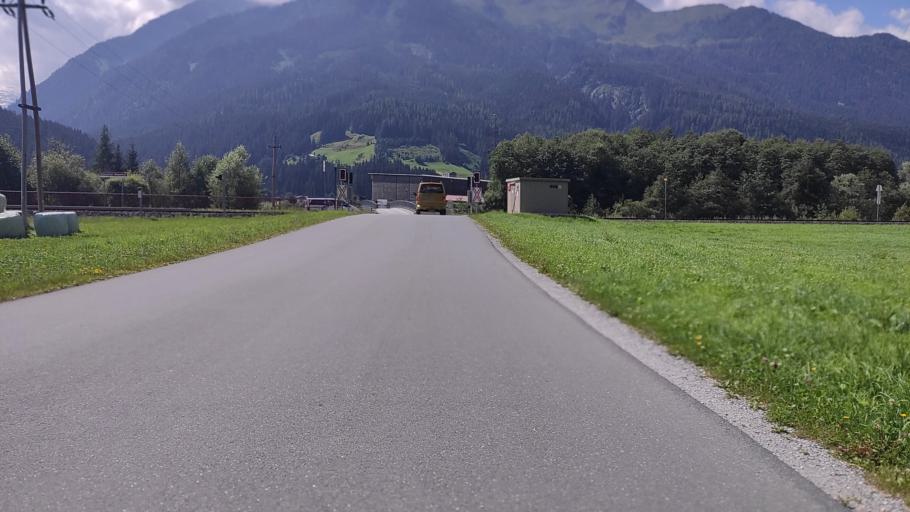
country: AT
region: Salzburg
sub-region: Politischer Bezirk Zell am See
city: Bramberg am Wildkogel
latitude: 47.2575
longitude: 12.3178
